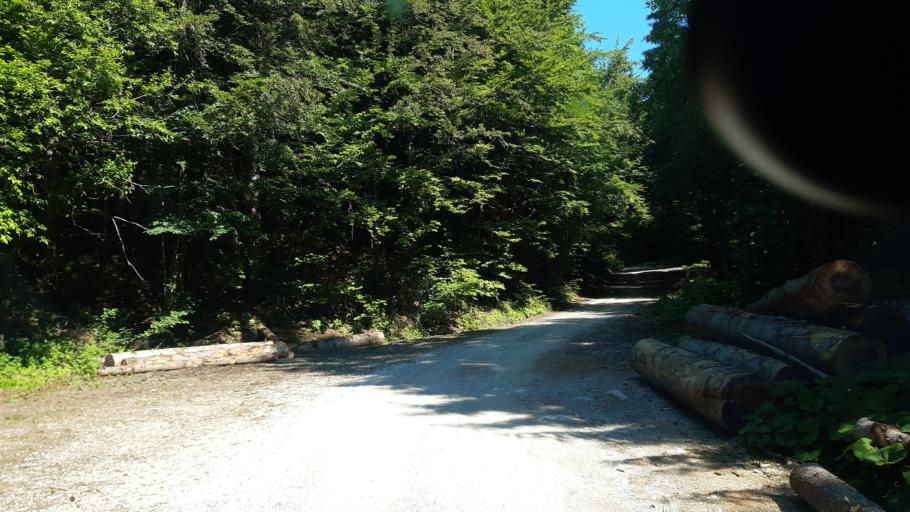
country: SI
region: Trzic
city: Bistrica pri Trzicu
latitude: 46.3700
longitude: 14.2760
